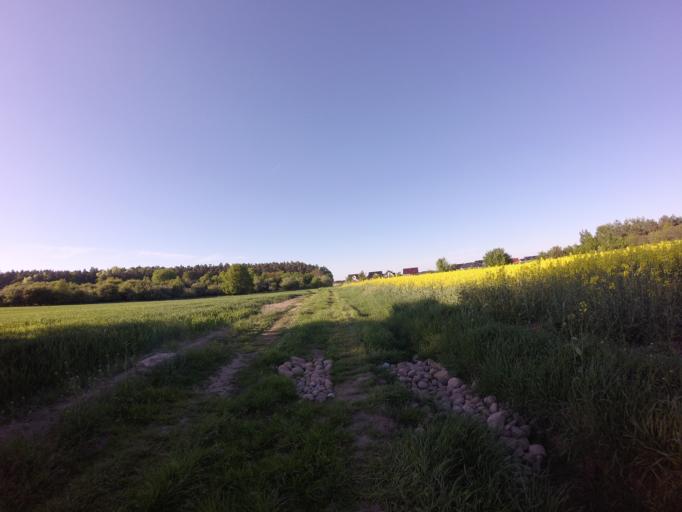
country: PL
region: West Pomeranian Voivodeship
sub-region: Powiat choszczenski
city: Choszczno
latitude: 53.1563
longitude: 15.3831
